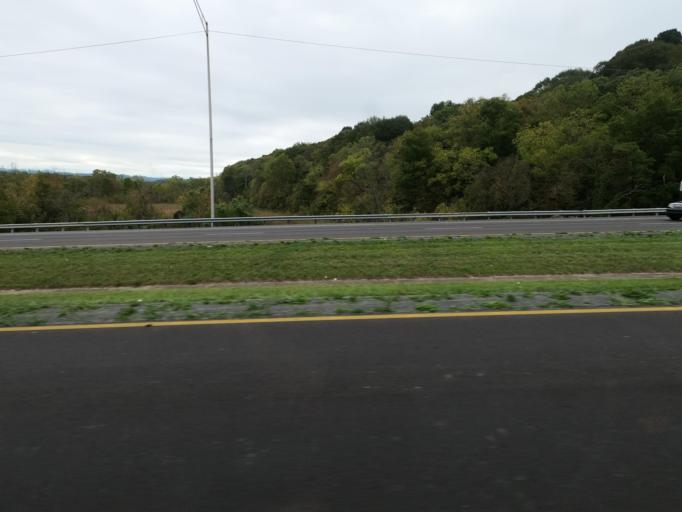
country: US
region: Tennessee
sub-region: Sullivan County
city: Bloomingdale
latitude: 36.5382
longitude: -82.5053
